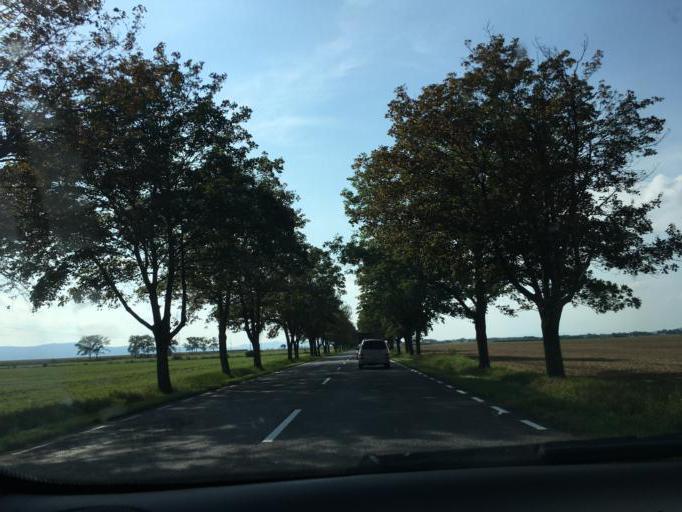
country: PL
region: Opole Voivodeship
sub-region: Powiat nyski
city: Paczkow
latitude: 50.4504
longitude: 17.0757
